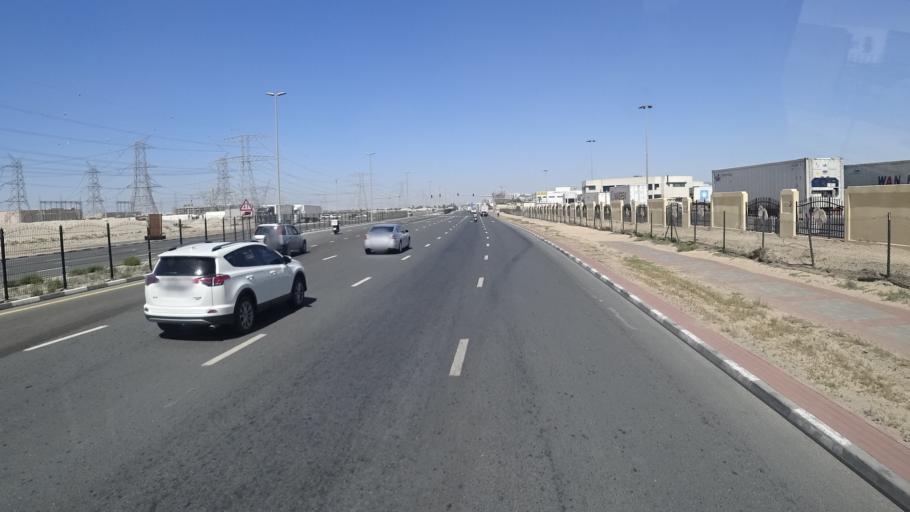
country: AE
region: Ash Shariqah
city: Sharjah
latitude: 25.1713
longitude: 55.3840
